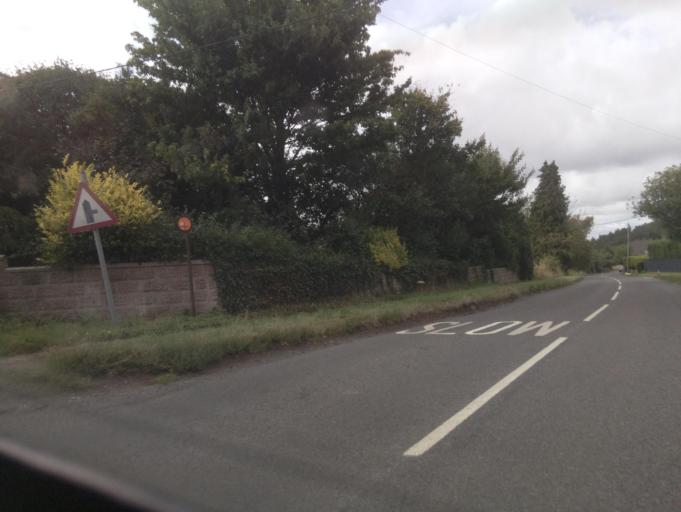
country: GB
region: England
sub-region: Shropshire
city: Woodcote
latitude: 52.7228
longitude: -2.3492
